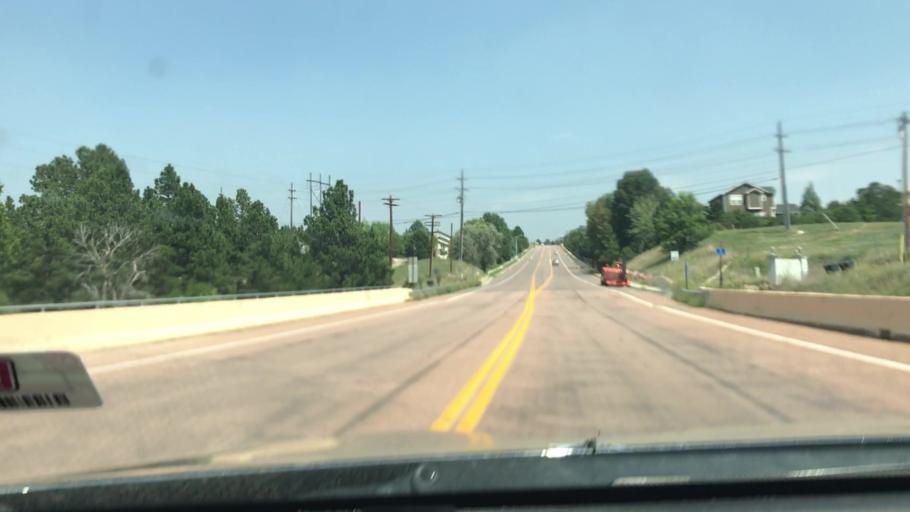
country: US
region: Colorado
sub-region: El Paso County
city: Gleneagle
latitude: 38.9809
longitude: -104.7851
